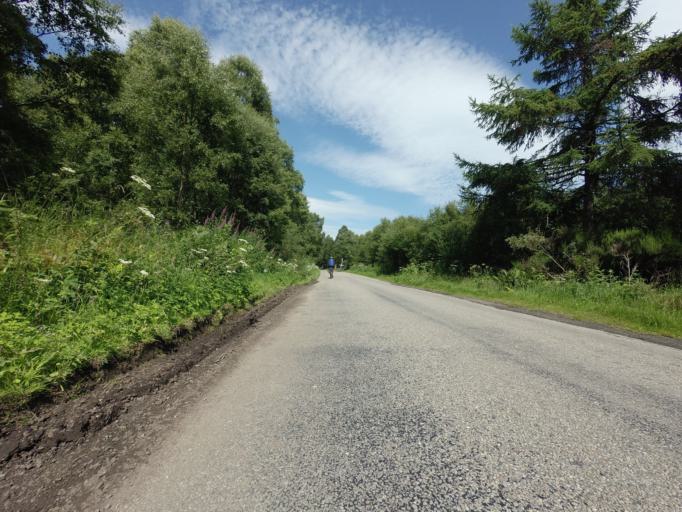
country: GB
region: Scotland
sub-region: Highland
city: Inverness
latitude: 57.5328
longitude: -4.3217
